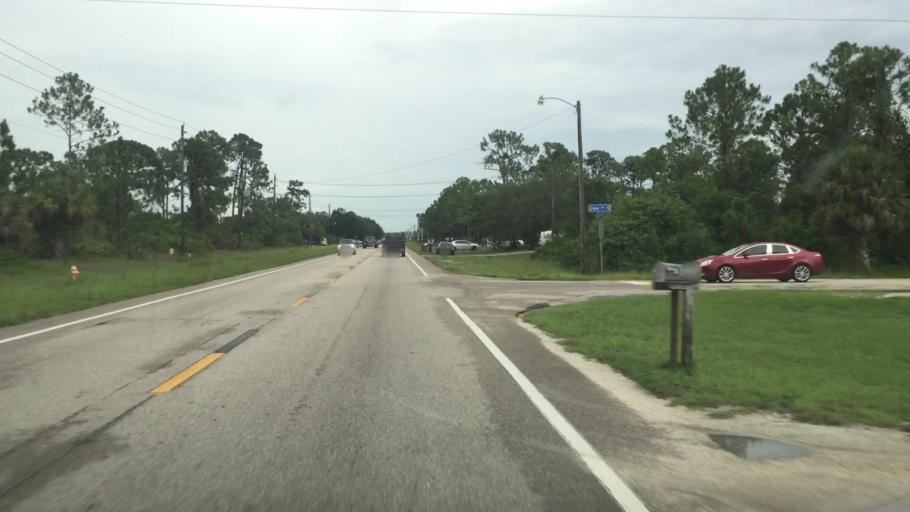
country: US
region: Florida
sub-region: Lee County
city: Gateway
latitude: 26.6056
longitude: -81.7405
